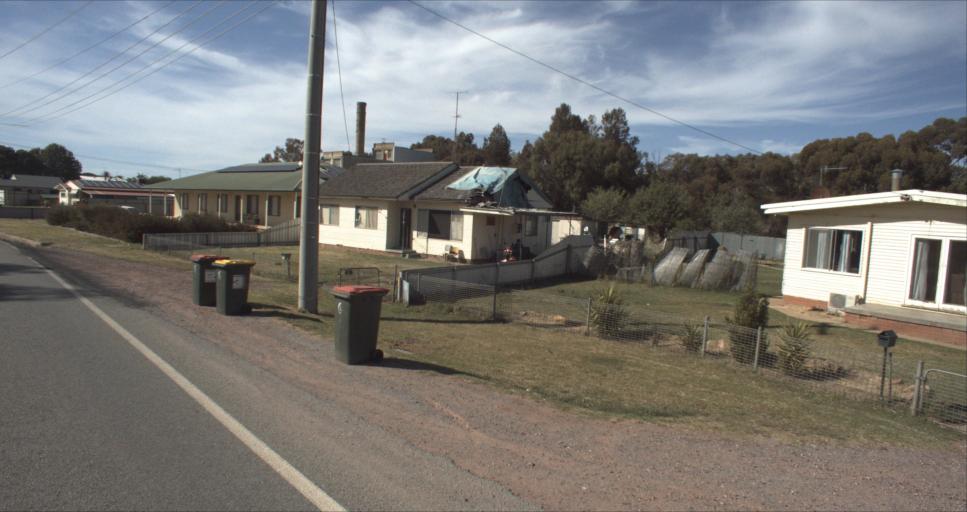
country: AU
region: New South Wales
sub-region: Leeton
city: Leeton
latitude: -34.6021
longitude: 146.4067
